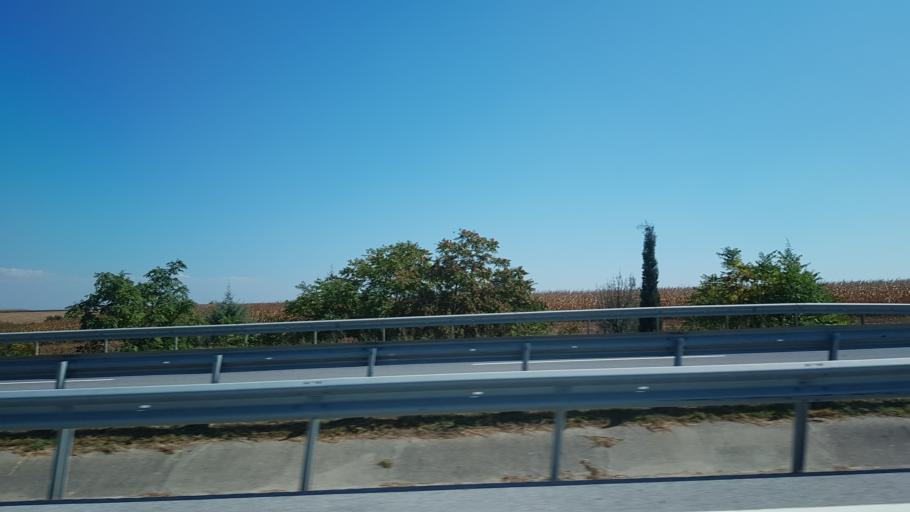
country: TR
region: Kirklareli
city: Inece
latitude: 41.5940
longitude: 27.1595
